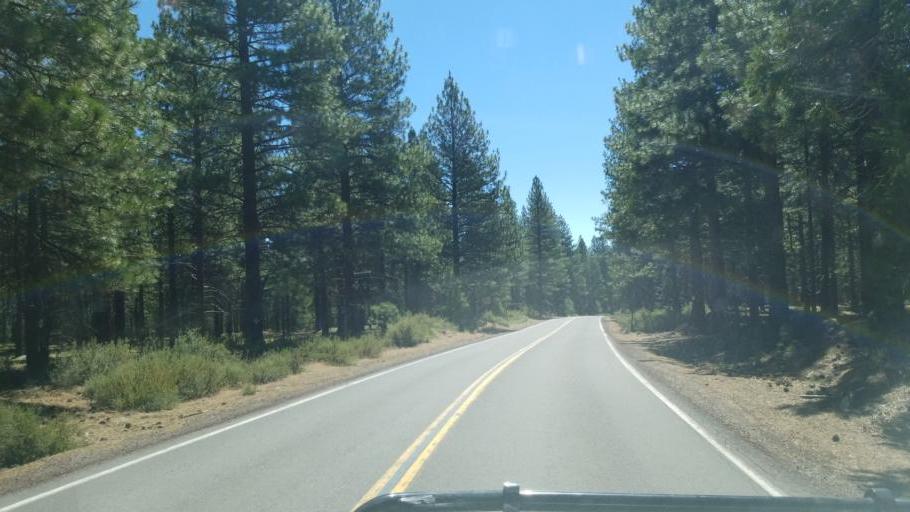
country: US
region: California
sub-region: Lassen County
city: Susanville
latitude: 40.4353
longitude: -120.7383
